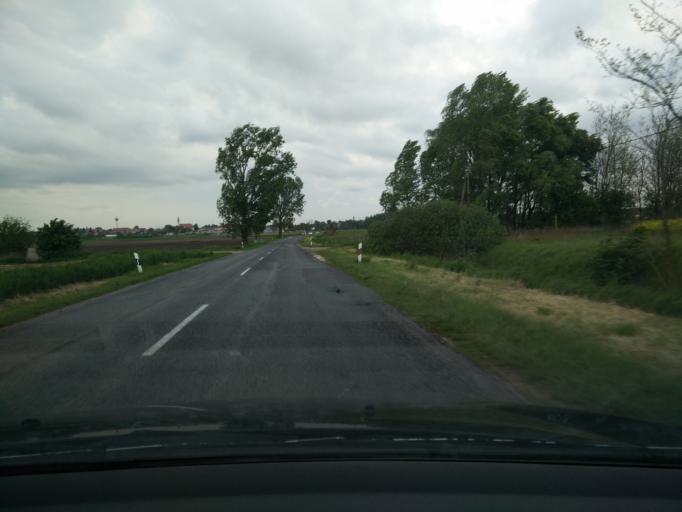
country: HU
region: Gyor-Moson-Sopron
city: Tet
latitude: 47.5043
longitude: 17.5094
